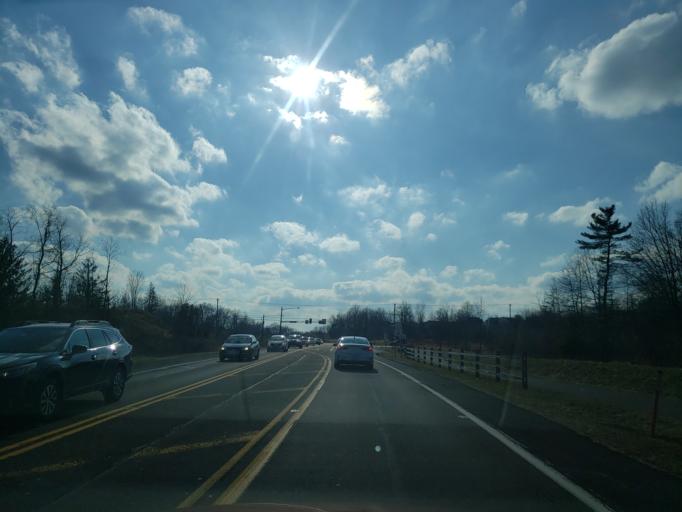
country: US
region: Pennsylvania
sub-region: Bucks County
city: New Britain
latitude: 40.2814
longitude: -75.1801
